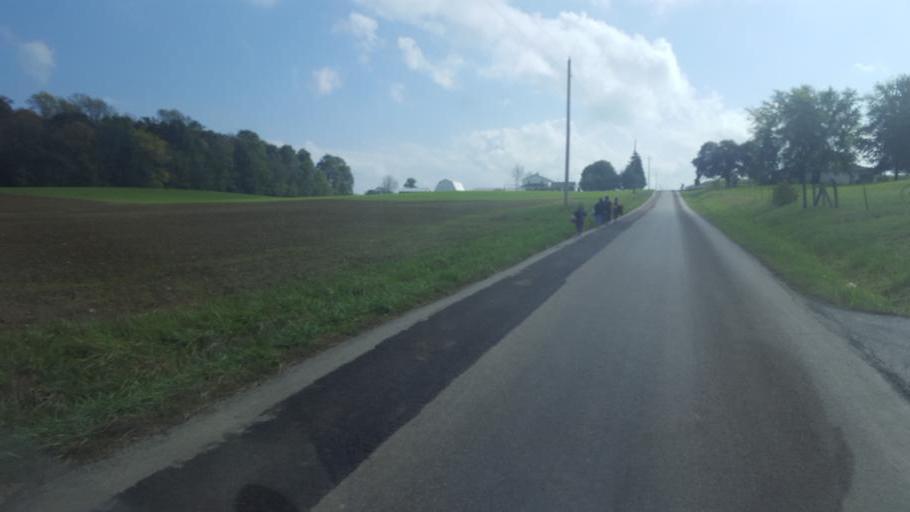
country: US
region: Ohio
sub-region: Holmes County
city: Millersburg
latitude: 40.6425
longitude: -81.8614
